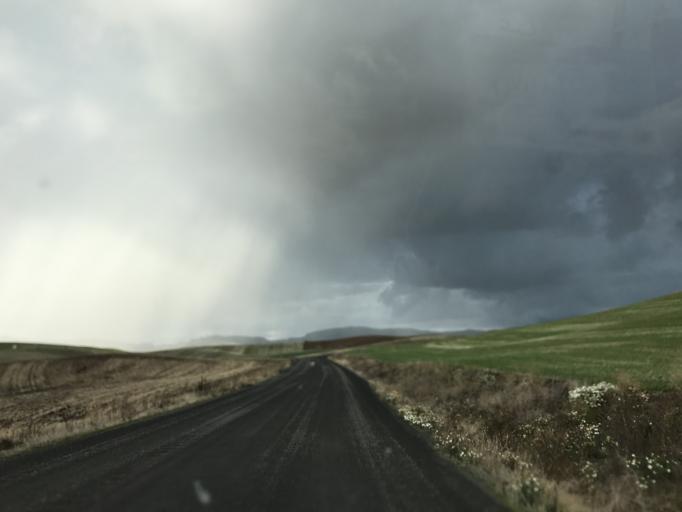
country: US
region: Idaho
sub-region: Latah County
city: Moscow
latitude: 46.7642
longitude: -116.9912
